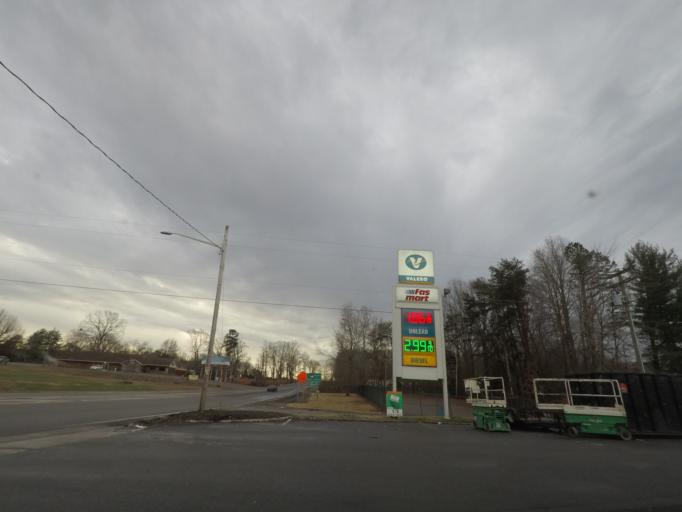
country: US
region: Virginia
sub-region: City of Danville
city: Danville
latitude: 36.5418
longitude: -79.4010
